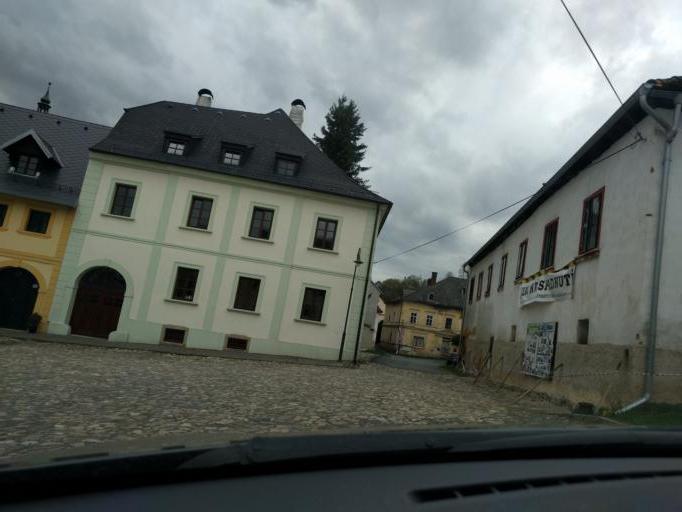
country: CZ
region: Plzensky
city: Bezdruzice
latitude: 49.9403
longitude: 13.0043
